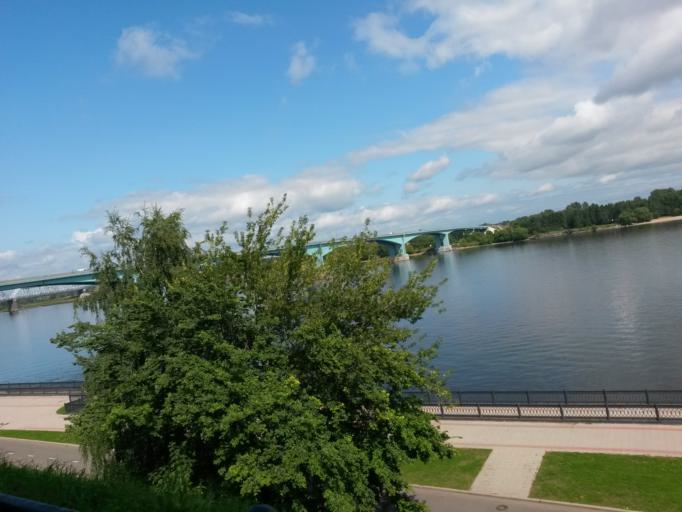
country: RU
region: Jaroslavl
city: Yaroslavl
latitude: 57.6375
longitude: 39.8899
